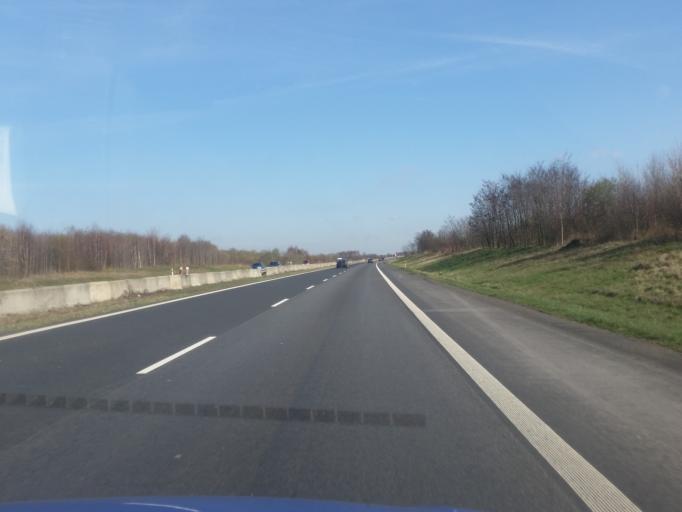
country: PL
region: Silesian Voivodeship
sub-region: Powiat czestochowski
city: Borowno
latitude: 50.9445
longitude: 19.2381
